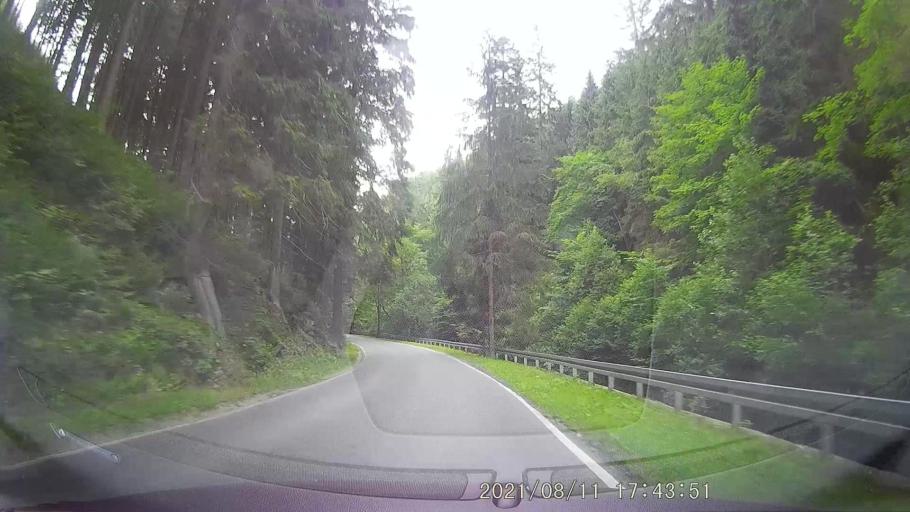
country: PL
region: Lower Silesian Voivodeship
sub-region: Powiat klodzki
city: Duszniki-Zdroj
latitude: 50.3820
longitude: 16.3893
